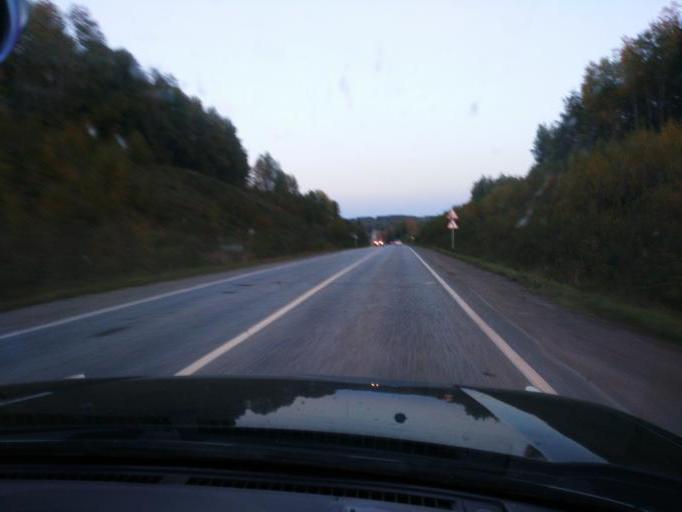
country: RU
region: Perm
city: Verkhnechusovskiye Gorodki
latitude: 58.2953
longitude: 56.8700
